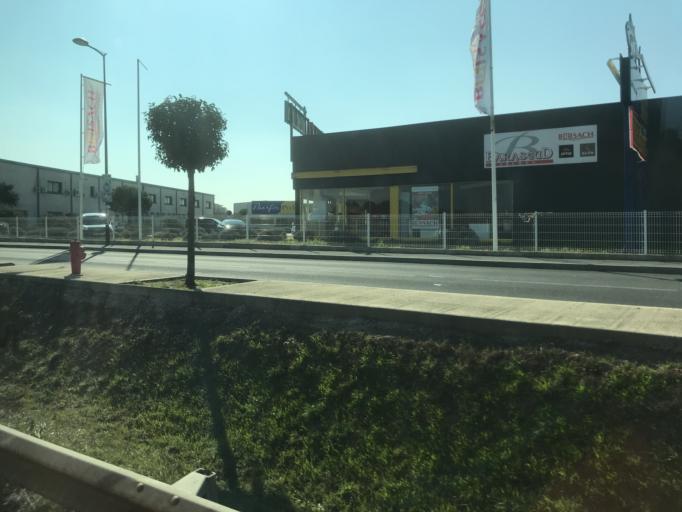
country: FR
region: Languedoc-Roussillon
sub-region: Departement de l'Herault
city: Perols
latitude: 43.5852
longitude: 3.9410
